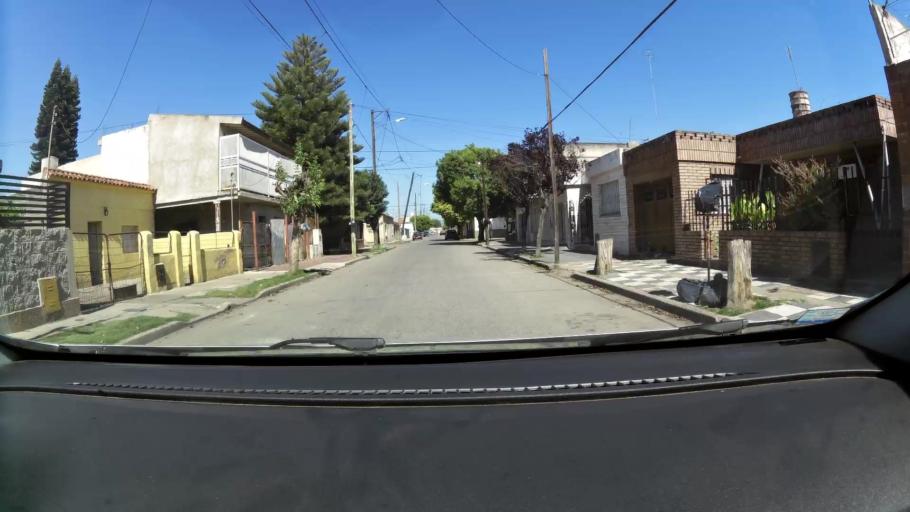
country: AR
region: Cordoba
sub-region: Departamento de Capital
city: Cordoba
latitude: -31.4398
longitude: -64.1362
